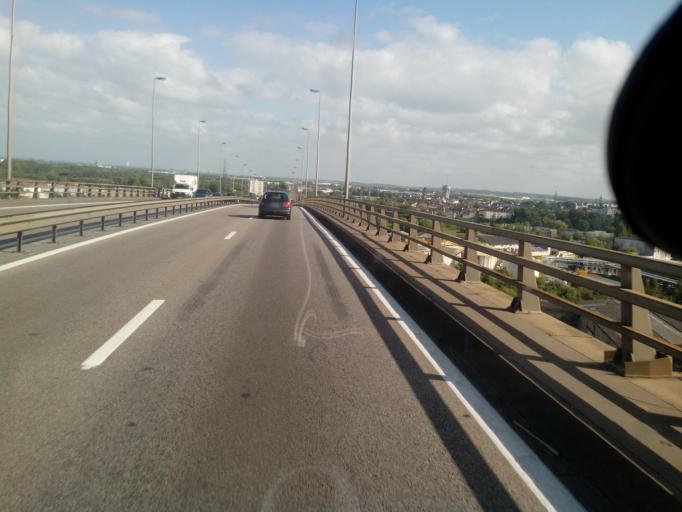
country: FR
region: Lower Normandy
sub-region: Departement du Calvados
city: Mondeville
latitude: 49.1859
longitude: -0.3293
